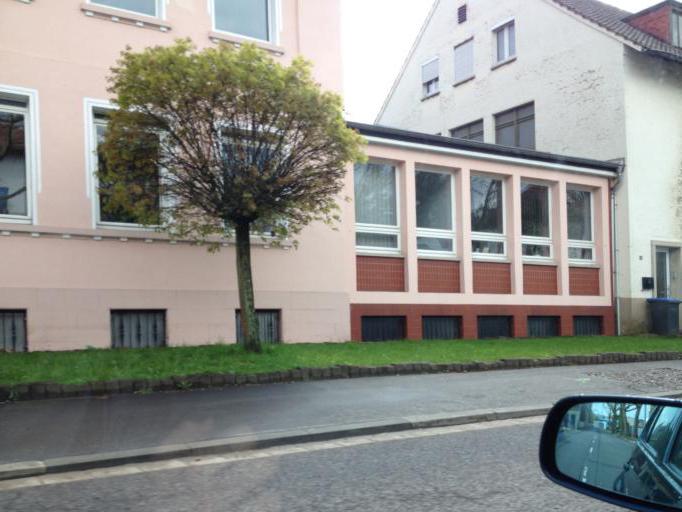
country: DE
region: Saarland
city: Homburg
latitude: 49.3173
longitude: 7.3256
